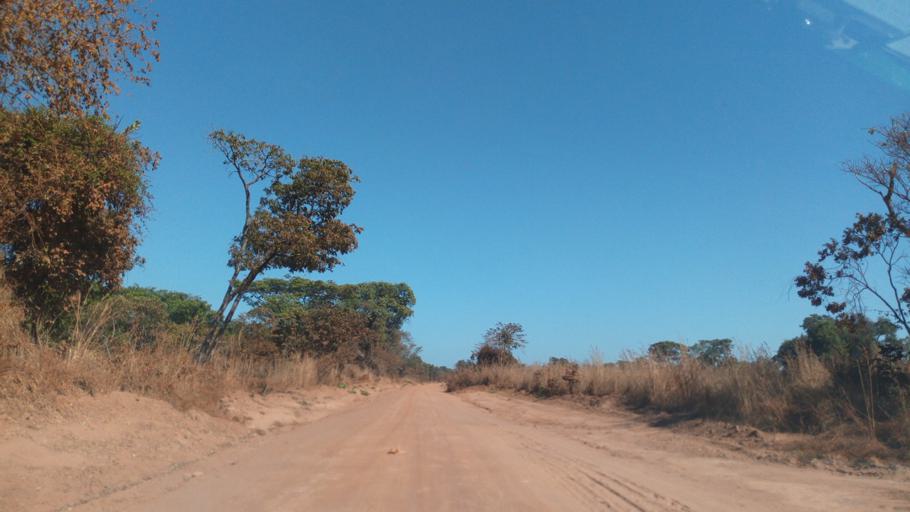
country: ZM
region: Luapula
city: Mwense
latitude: -10.7548
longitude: 28.3177
